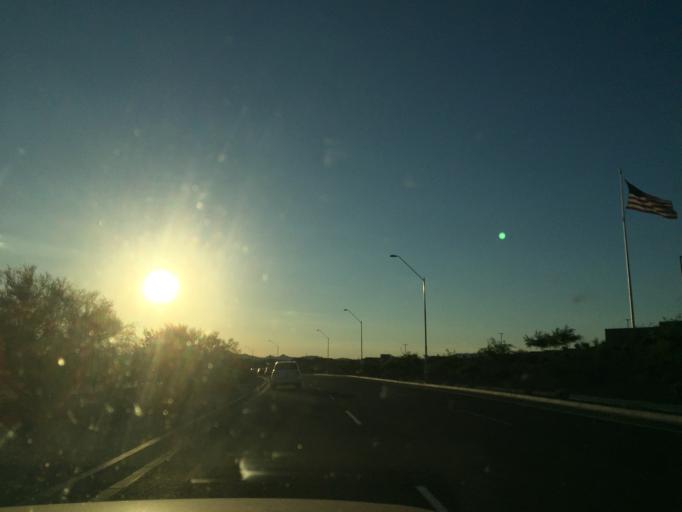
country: US
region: Arizona
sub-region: Maricopa County
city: Sun City West
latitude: 33.7130
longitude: -112.2790
